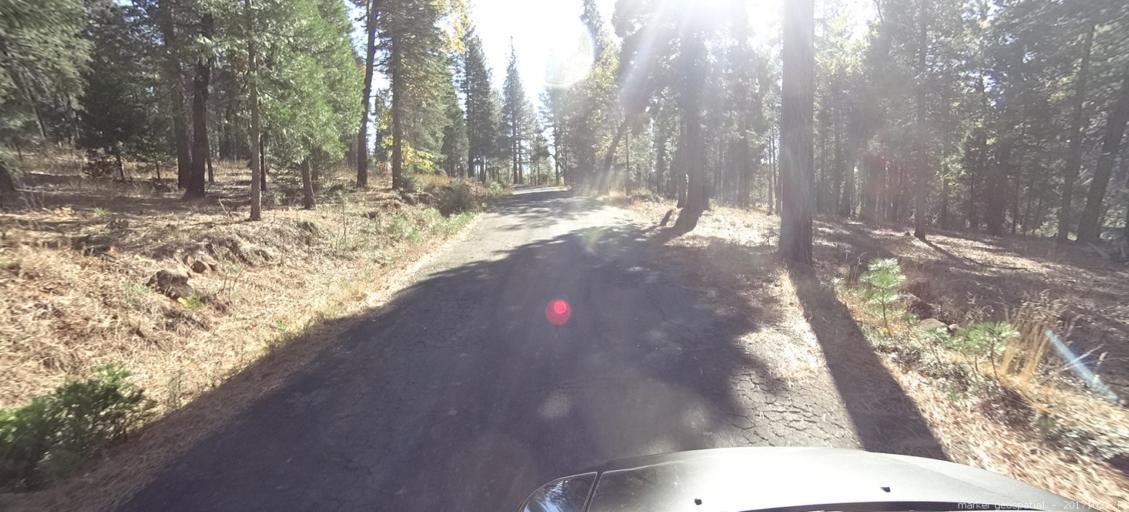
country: US
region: California
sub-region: Shasta County
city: Shingletown
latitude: 40.6167
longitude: -121.8373
